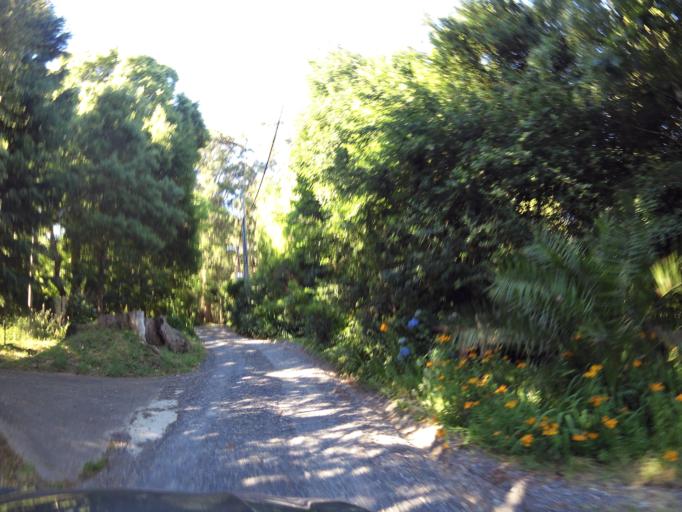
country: AU
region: Victoria
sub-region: Yarra Ranges
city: Ferny Creek
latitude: -37.8810
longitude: 145.3373
